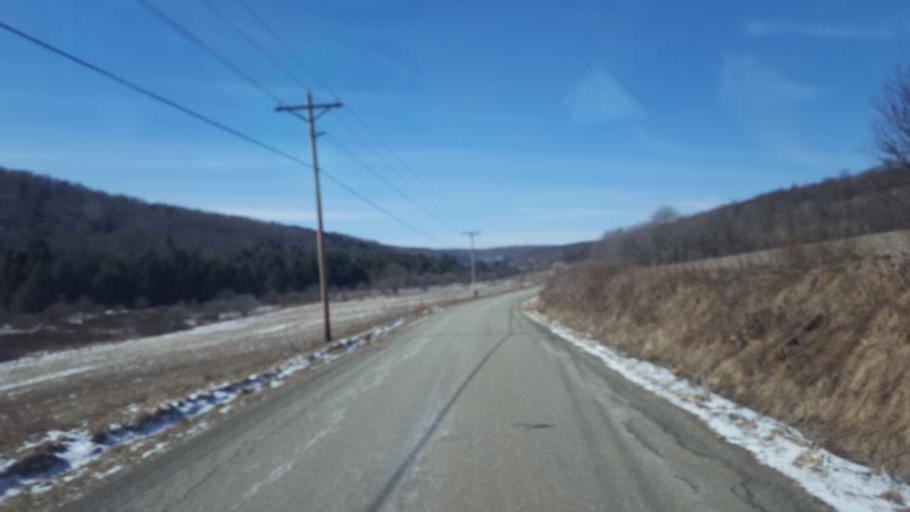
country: US
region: New York
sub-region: Allegany County
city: Andover
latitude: 41.9497
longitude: -77.7863
